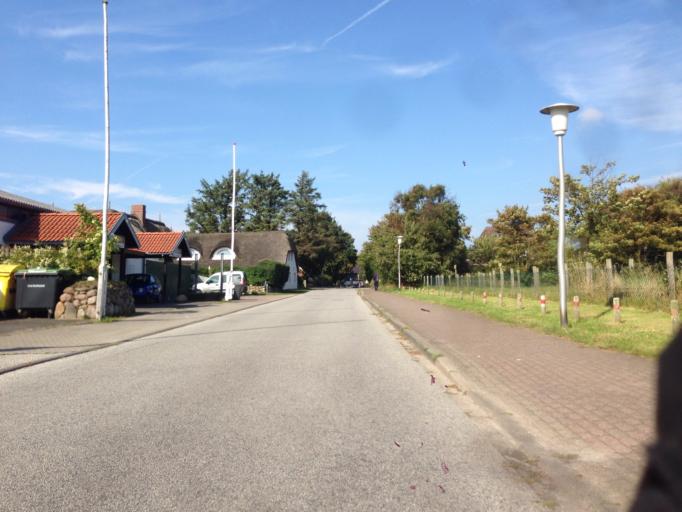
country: DE
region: Schleswig-Holstein
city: Westerland
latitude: 54.9071
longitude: 8.3188
